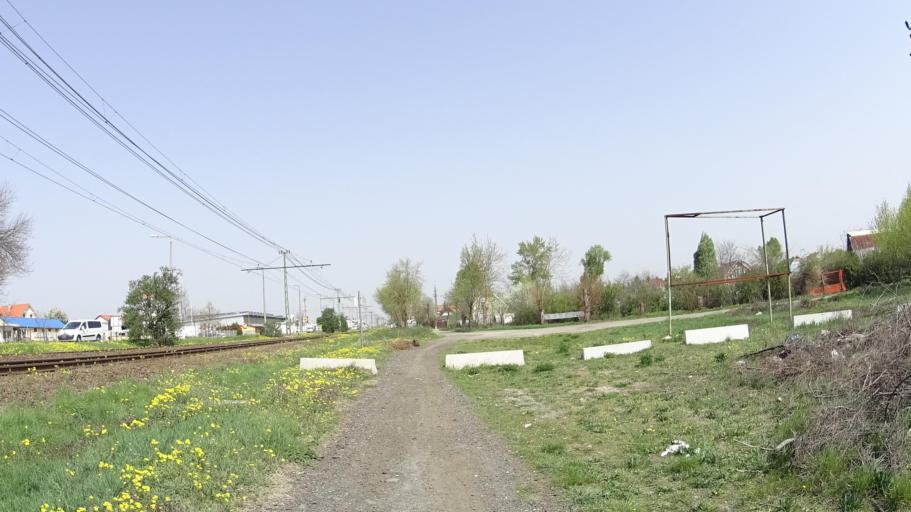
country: HU
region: Budapest
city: Budapest XXIII. keruelet
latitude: 47.3833
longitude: 19.1081
